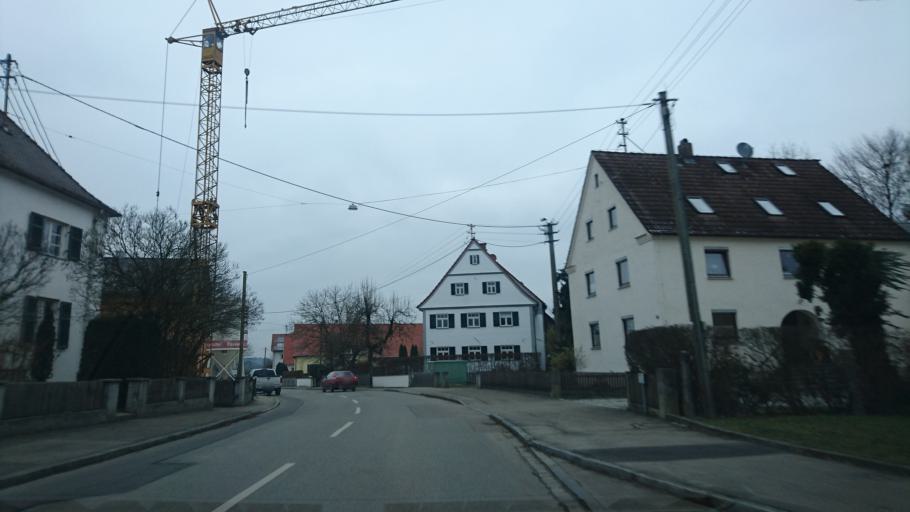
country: DE
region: Bavaria
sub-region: Swabia
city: Altenmunster
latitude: 48.4378
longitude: 10.5959
